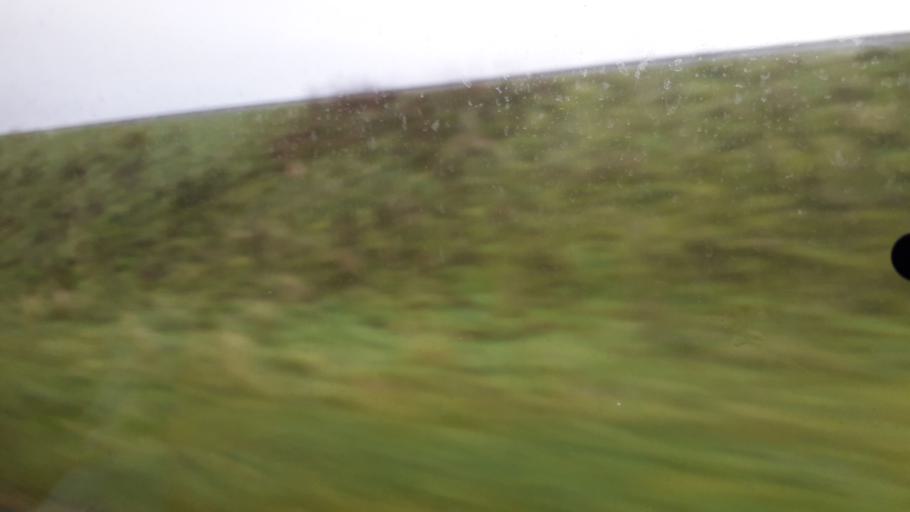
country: IE
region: Connaught
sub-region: County Galway
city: Athenry
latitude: 53.2931
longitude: -8.8085
